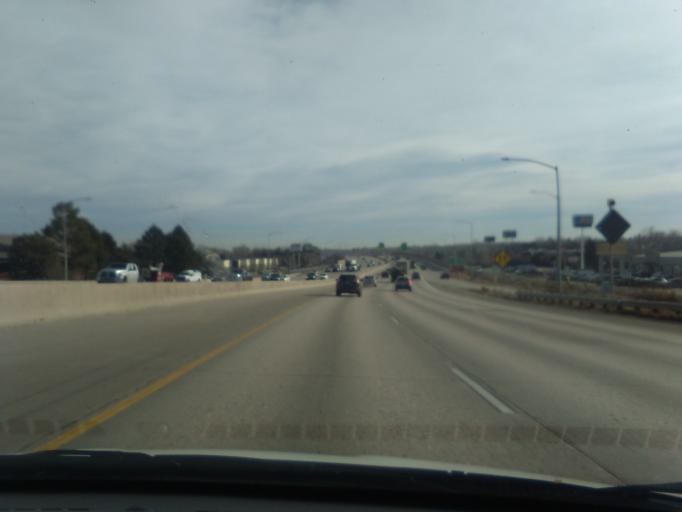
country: US
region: Colorado
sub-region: Jefferson County
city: Arvada
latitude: 39.7840
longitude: -105.1075
